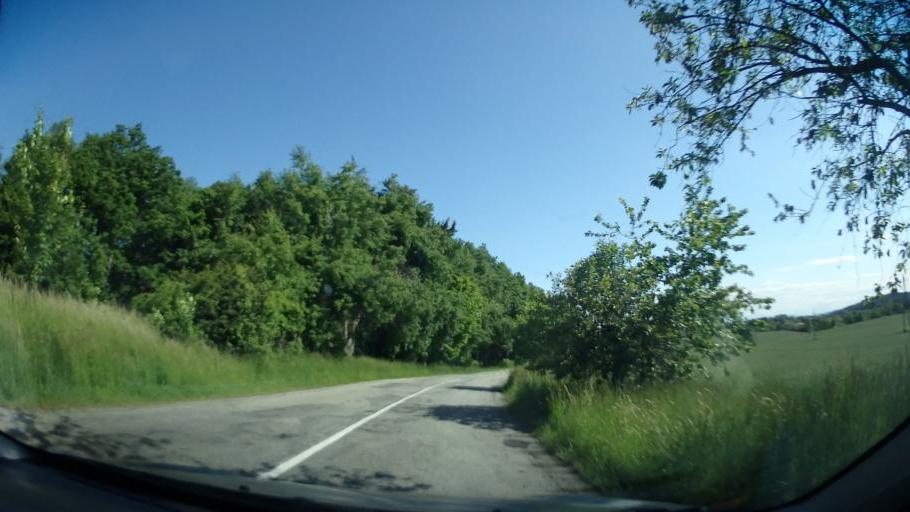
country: CZ
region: South Moravian
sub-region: Okres Blansko
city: Letovice
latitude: 49.6026
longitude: 16.6071
